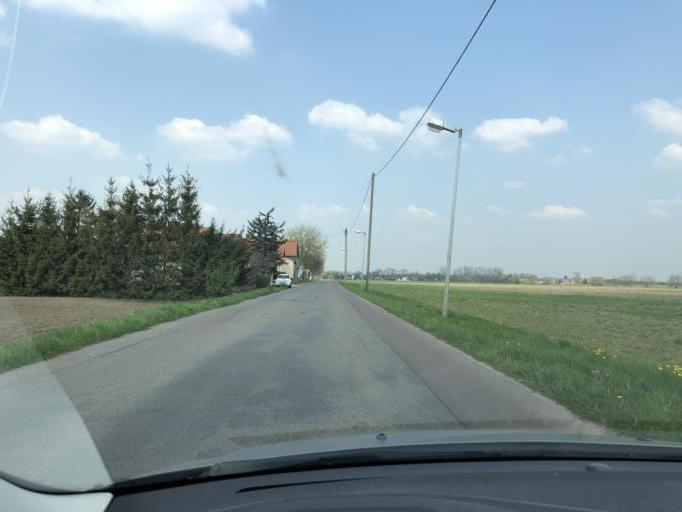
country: DE
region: Saxony-Anhalt
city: Landsberg
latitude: 51.5534
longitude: 12.1322
